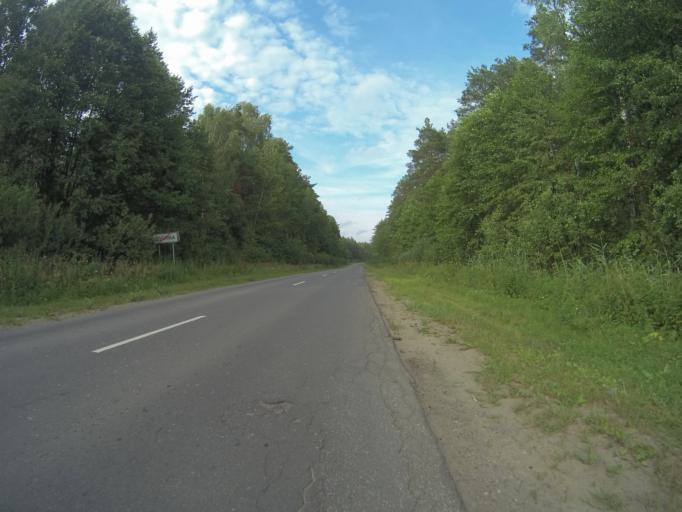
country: RU
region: Vladimir
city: Vorsha
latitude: 56.0026
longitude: 40.0696
